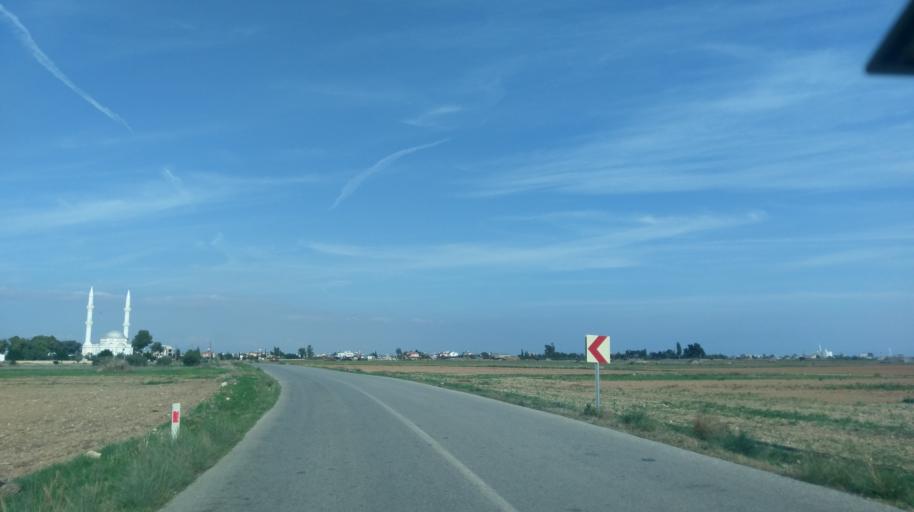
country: CY
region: Ammochostos
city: Acheritou
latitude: 35.1907
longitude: 33.8549
